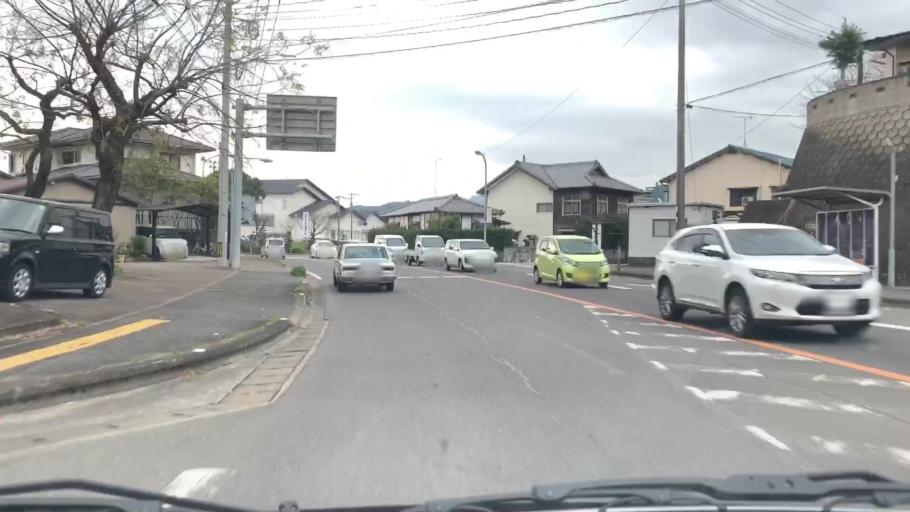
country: JP
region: Saga Prefecture
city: Kashima
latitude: 33.1321
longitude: 130.0614
